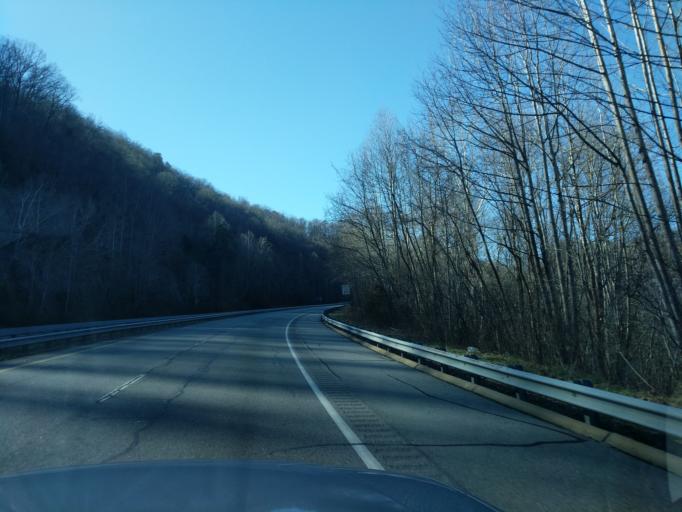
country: US
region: North Carolina
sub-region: Swain County
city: Bryson City
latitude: 35.4272
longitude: -83.4058
